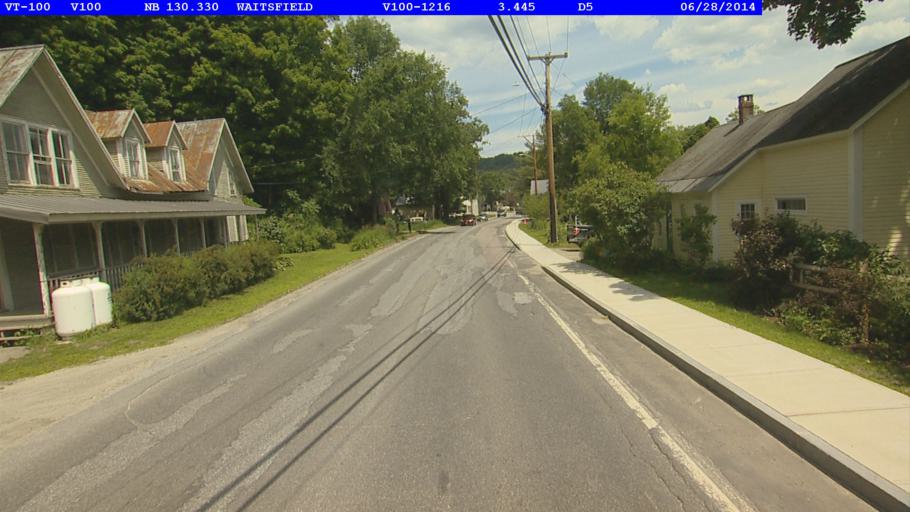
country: US
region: Vermont
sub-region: Washington County
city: Waterbury
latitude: 44.1888
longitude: -72.8279
